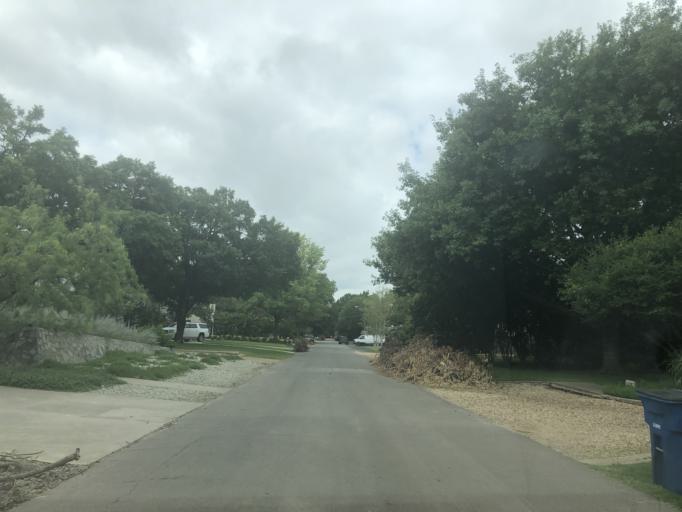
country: US
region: Texas
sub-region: Dallas County
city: University Park
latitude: 32.8545
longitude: -96.8337
